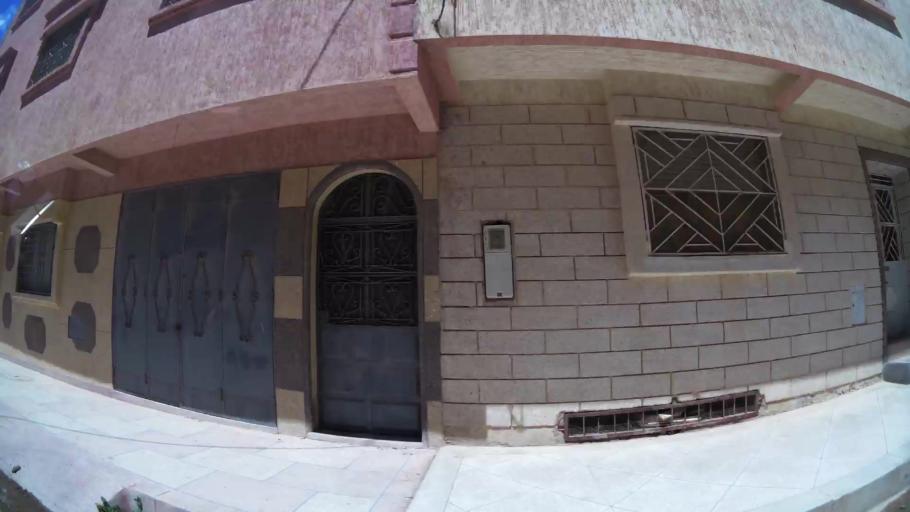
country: MA
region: Oriental
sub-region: Oujda-Angad
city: Oujda
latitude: 34.6573
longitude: -1.9274
